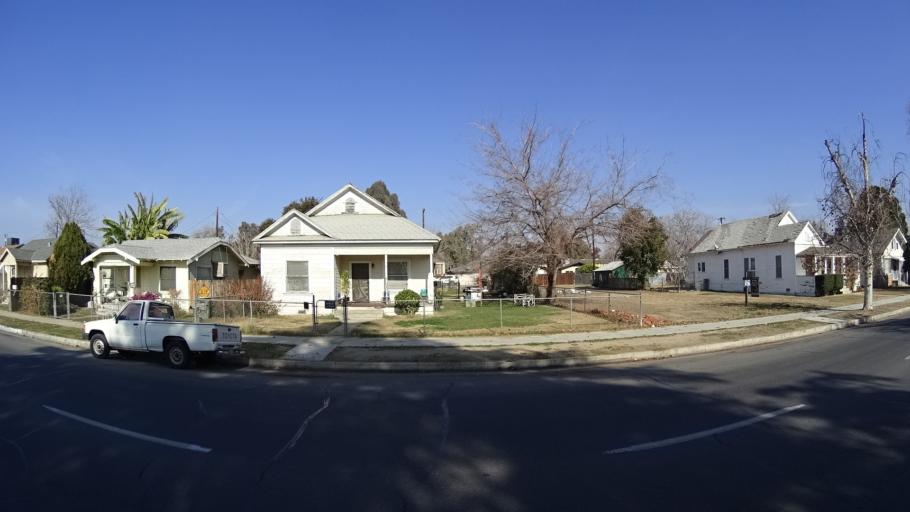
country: US
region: California
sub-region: Kern County
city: Bakersfield
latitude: 35.3826
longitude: -118.9935
